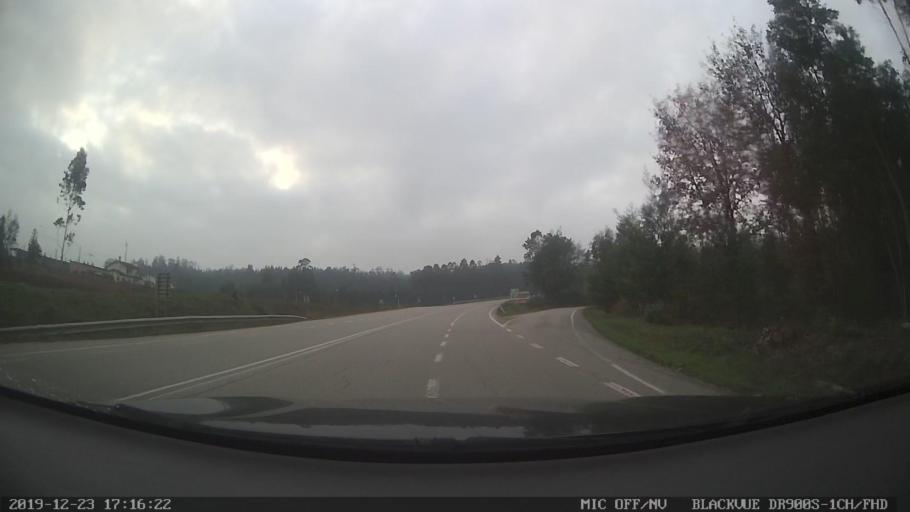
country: PT
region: Viseu
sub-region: Mortagua
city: Mortagua
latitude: 40.3935
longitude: -8.2532
